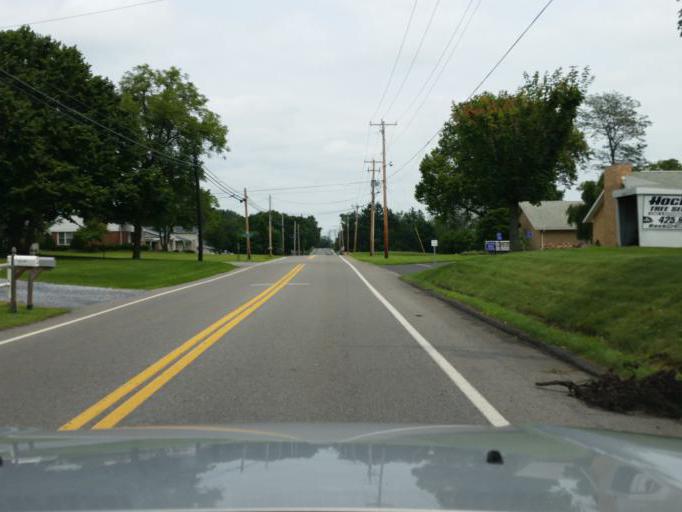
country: US
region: Pennsylvania
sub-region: Dauphin County
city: Colonial Park
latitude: 40.2845
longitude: -76.7933
